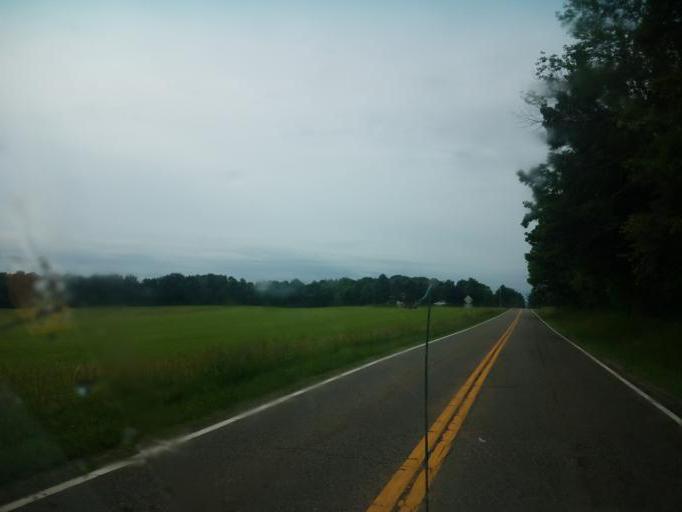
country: US
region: Ohio
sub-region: Columbiana County
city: Salem
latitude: 40.8108
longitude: -80.8583
